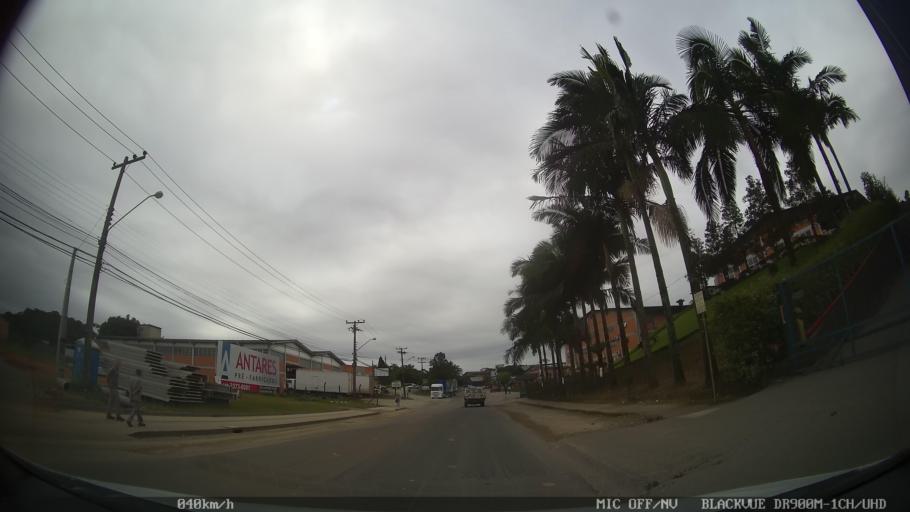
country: BR
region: Santa Catarina
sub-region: Joinville
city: Joinville
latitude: -26.2612
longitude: -48.8838
